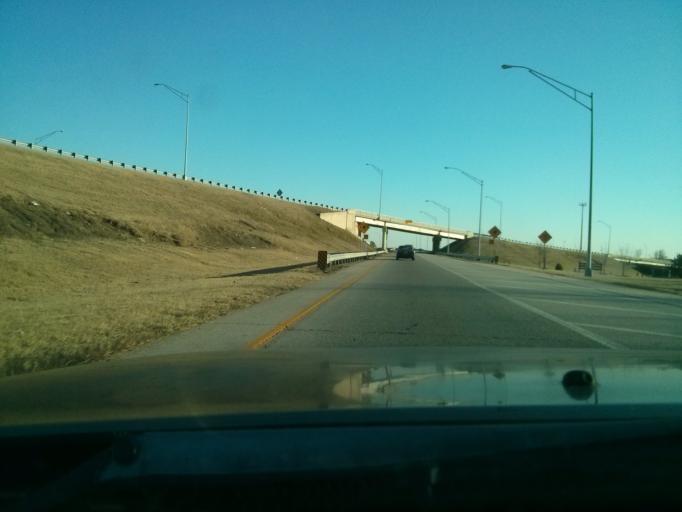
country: US
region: Oklahoma
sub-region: Tulsa County
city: Owasso
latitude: 36.1655
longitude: -95.8833
